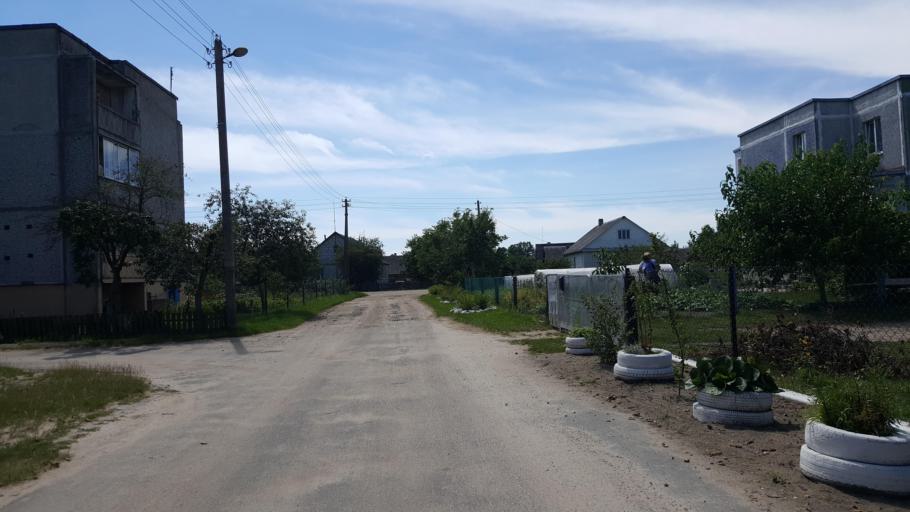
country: BY
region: Brest
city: Pruzhany
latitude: 52.5598
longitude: 24.2127
